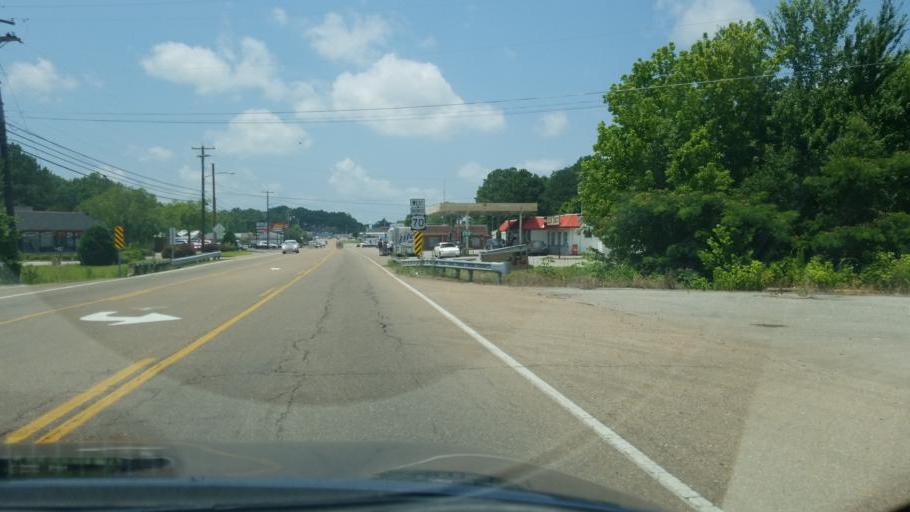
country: US
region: Tennessee
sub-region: Carroll County
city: Huntingdon
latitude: 36.0069
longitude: -88.4075
